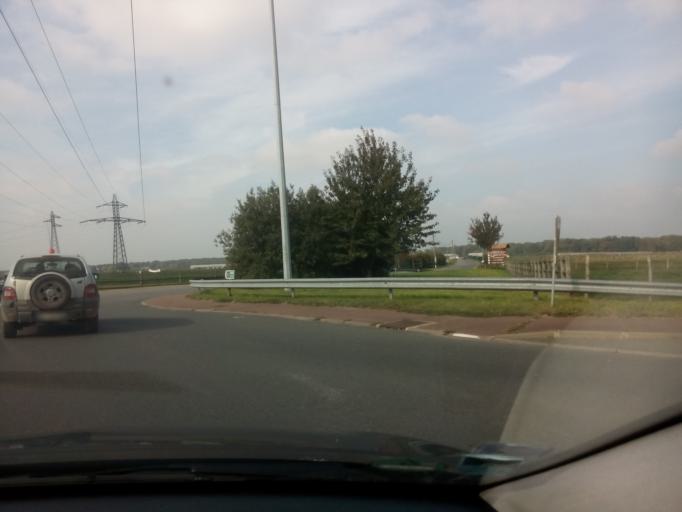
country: FR
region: Ile-de-France
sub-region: Departement des Yvelines
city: Jouy-en-Josas
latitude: 48.7504
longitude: 2.1662
